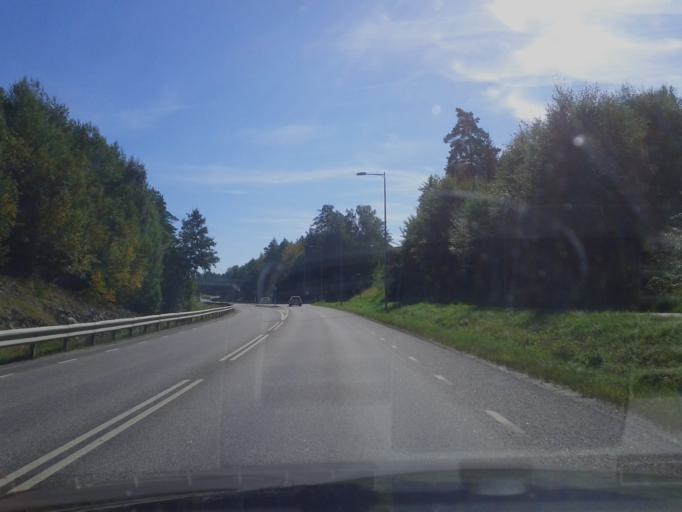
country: SE
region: Stockholm
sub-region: Taby Kommun
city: Taby
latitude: 59.4663
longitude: 18.0580
